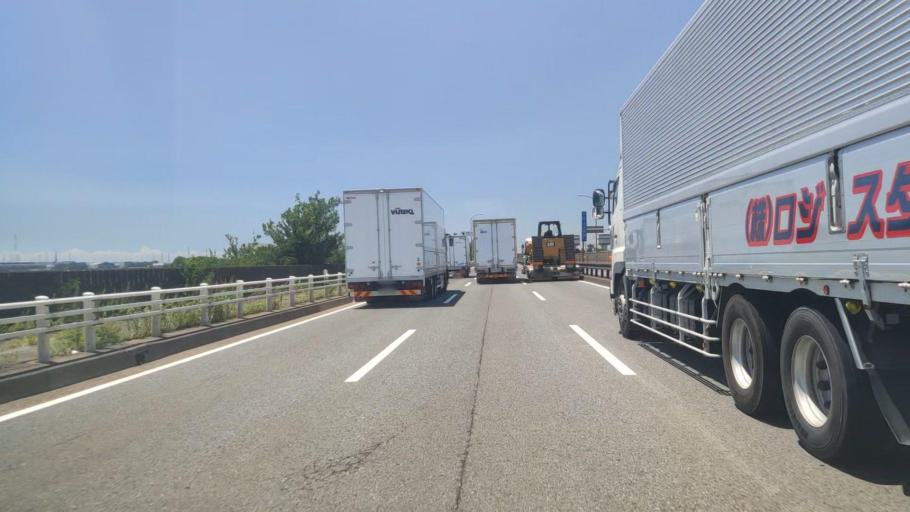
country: JP
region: Aichi
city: Kanie
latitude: 35.0819
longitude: 136.8258
